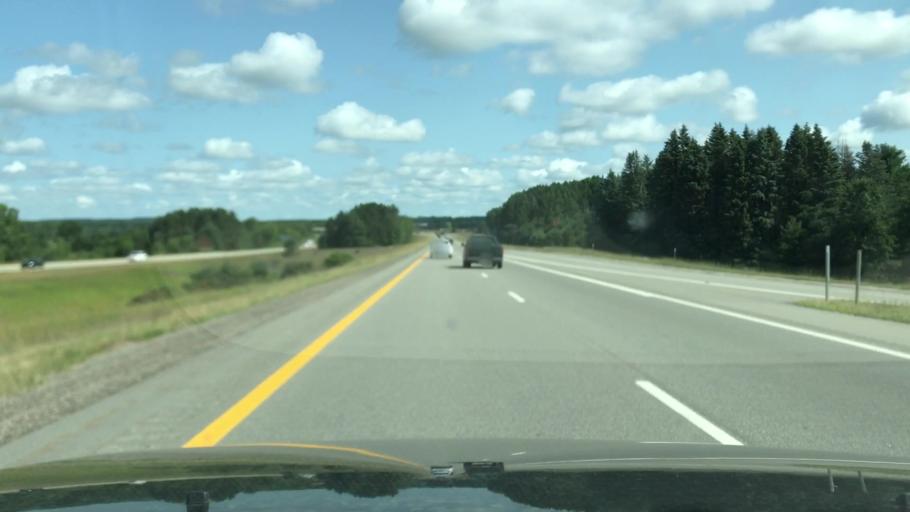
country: US
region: Michigan
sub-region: Mecosta County
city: Big Rapids
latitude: 43.5872
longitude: -85.4883
